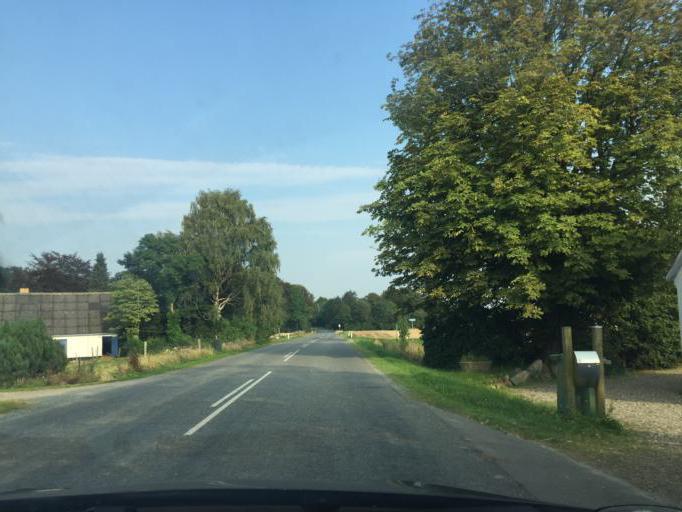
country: DK
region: South Denmark
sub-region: Faaborg-Midtfyn Kommune
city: Arslev
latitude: 55.2804
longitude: 10.5036
